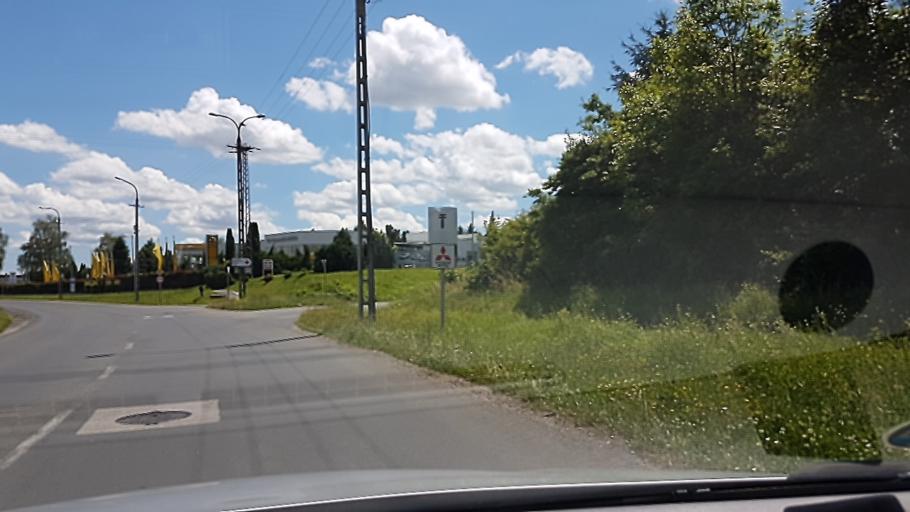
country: HU
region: Zala
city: Zalaegerszeg
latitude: 46.8539
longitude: 16.8087
